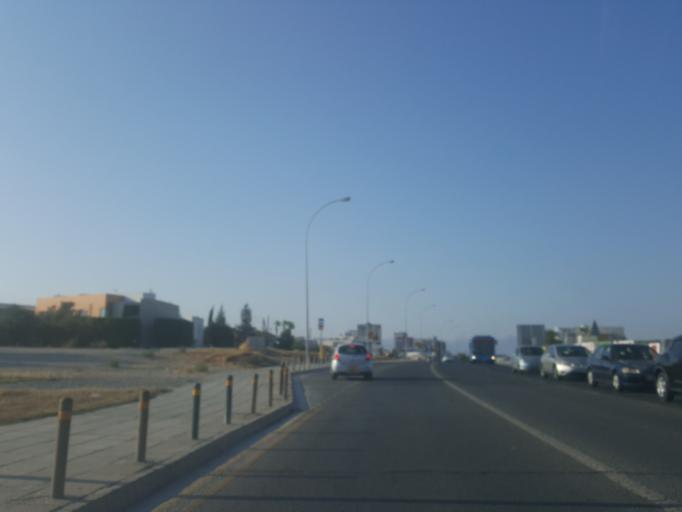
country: CY
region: Lefkosia
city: Nicosia
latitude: 35.1283
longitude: 33.3565
